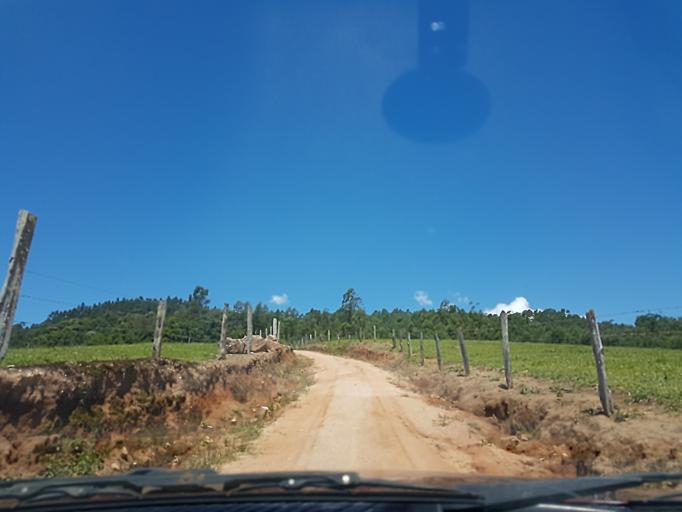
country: BR
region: Santa Catarina
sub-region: Braco Do Norte
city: Braco do Norte
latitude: -28.3874
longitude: -49.1276
